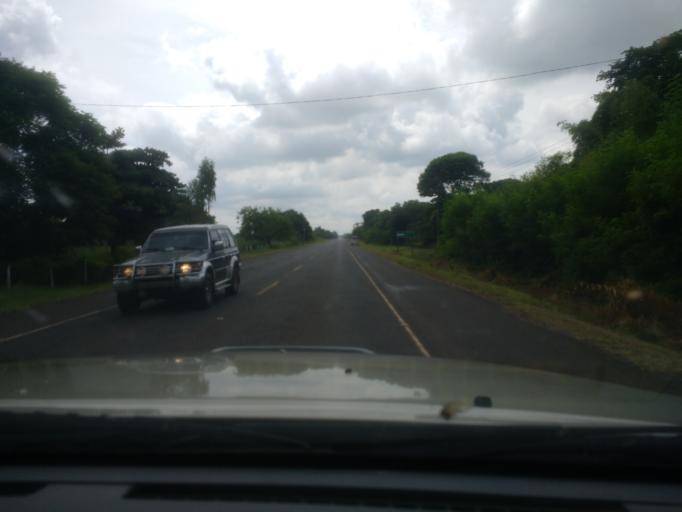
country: PY
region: San Pedro
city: Puerto Rosario
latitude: -24.4266
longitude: -57.0743
